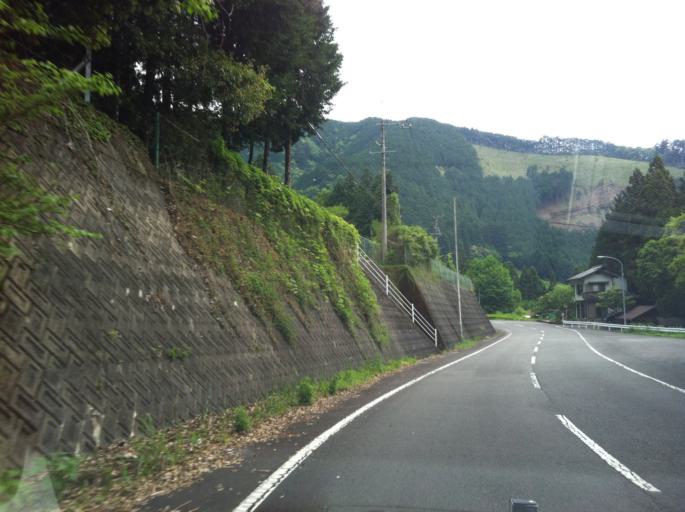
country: JP
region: Shizuoka
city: Shizuoka-shi
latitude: 35.1648
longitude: 138.3259
